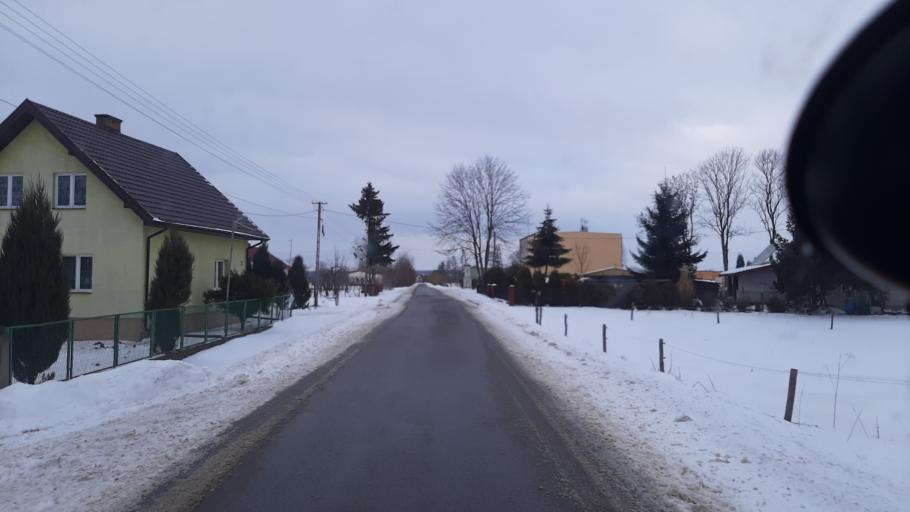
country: PL
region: Lublin Voivodeship
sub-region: Powiat lubartowski
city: Abramow
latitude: 51.4429
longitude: 22.2799
